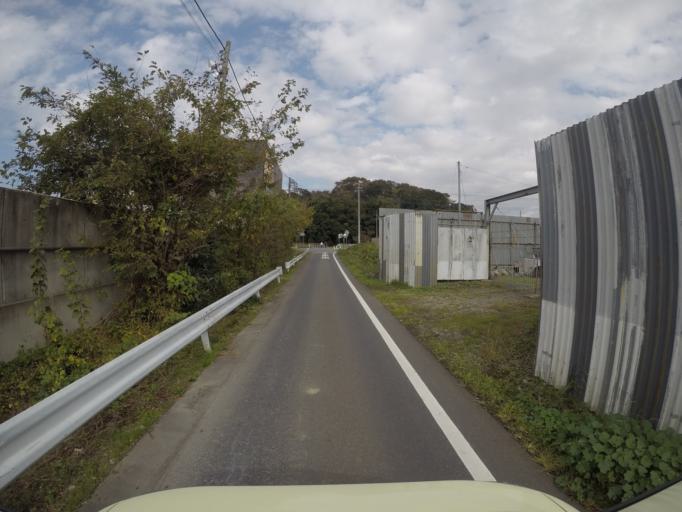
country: JP
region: Ibaraki
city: Iwai
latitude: 35.9921
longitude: 139.9001
